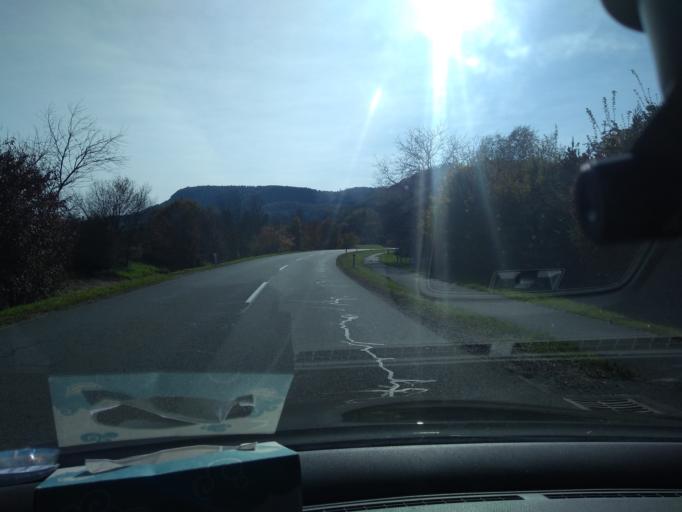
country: AT
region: Styria
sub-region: Politischer Bezirk Leibnitz
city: Wildon
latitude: 46.8947
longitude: 15.5196
